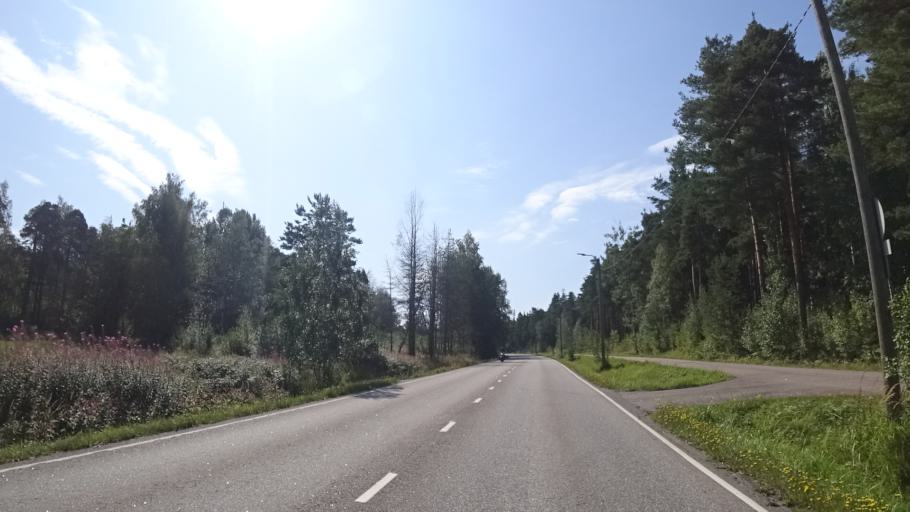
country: FI
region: Kymenlaakso
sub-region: Kotka-Hamina
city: Karhula
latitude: 60.5061
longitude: 26.9631
